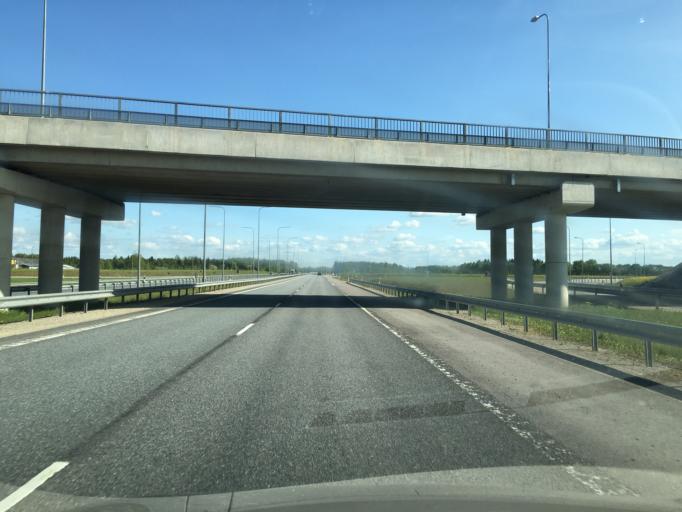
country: EE
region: Harju
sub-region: Rae vald
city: Vaida
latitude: 59.2519
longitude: 25.0140
